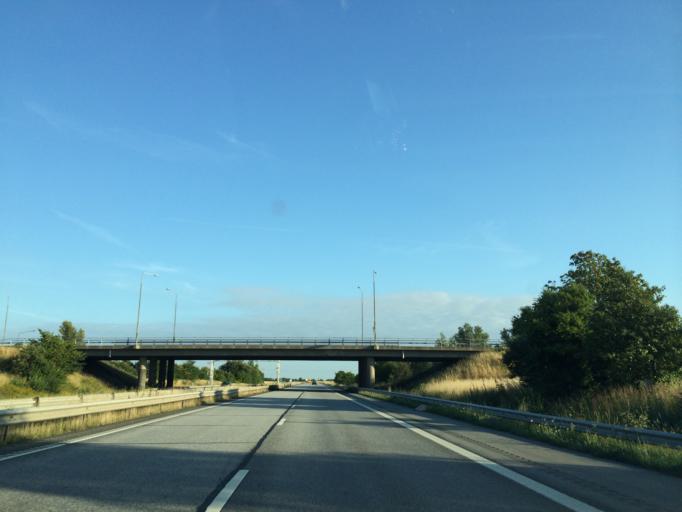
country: SE
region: Skane
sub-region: Malmo
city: Tygelsjo
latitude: 55.5311
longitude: 13.0072
